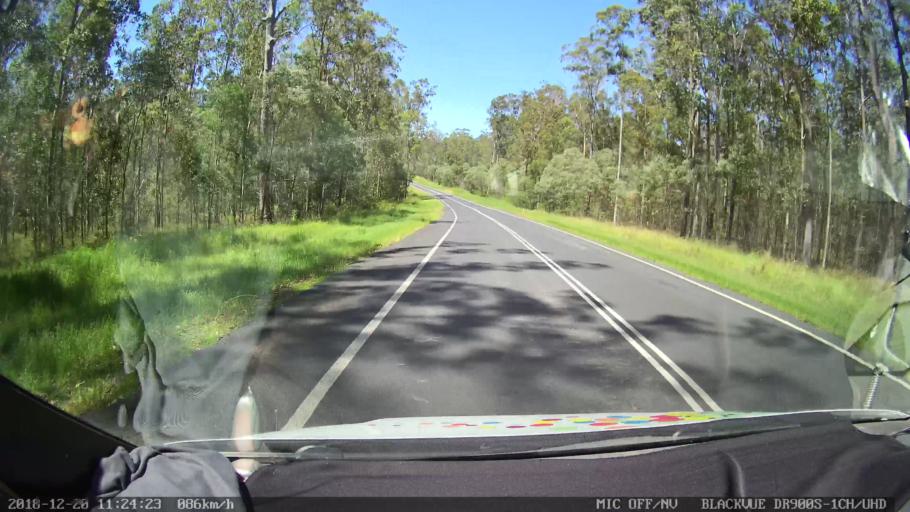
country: AU
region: New South Wales
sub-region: Richmond Valley
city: Casino
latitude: -29.0734
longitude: 153.0023
